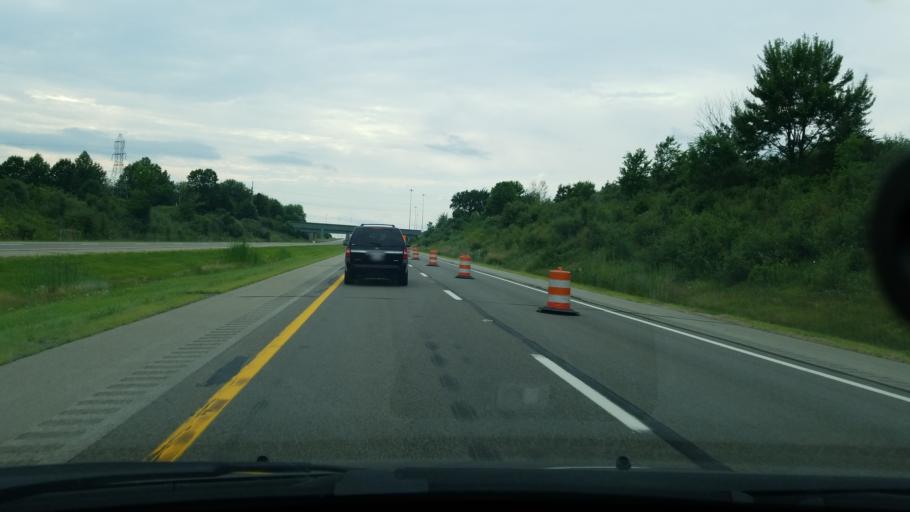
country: US
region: Ohio
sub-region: Mahoning County
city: Boardman
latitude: 40.9617
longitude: -80.6477
